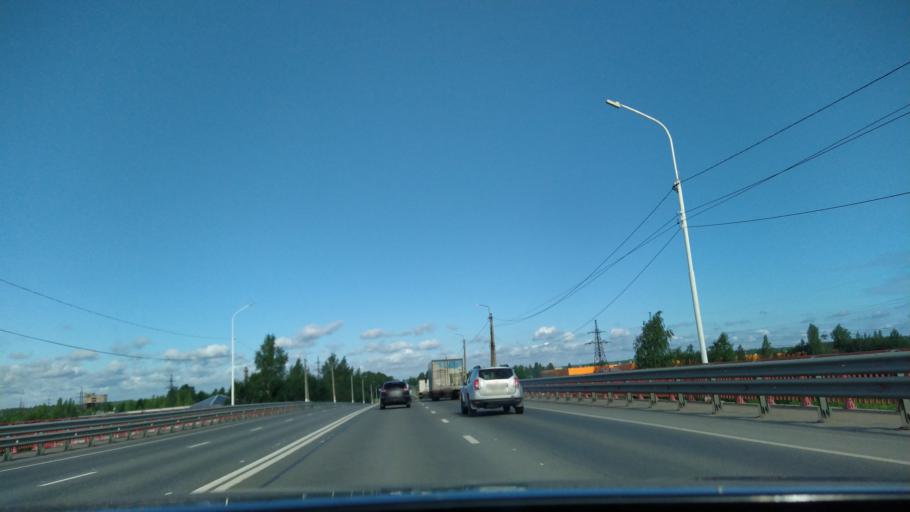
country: RU
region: Leningrad
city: Tosno
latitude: 59.5514
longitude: 30.8579
